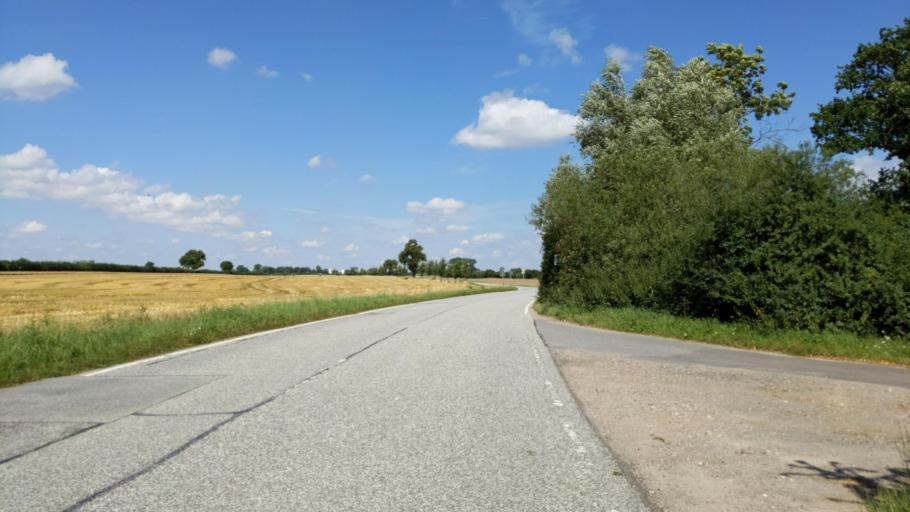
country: DE
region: Schleswig-Holstein
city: Krummesse
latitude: 53.8165
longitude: 10.6736
